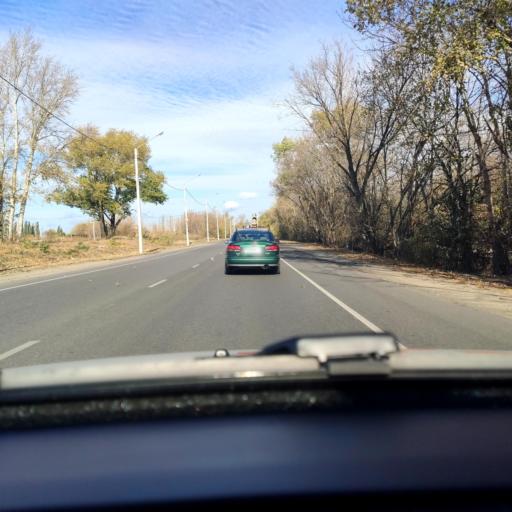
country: RU
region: Voronezj
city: Voronezh
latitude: 51.6122
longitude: 39.1792
